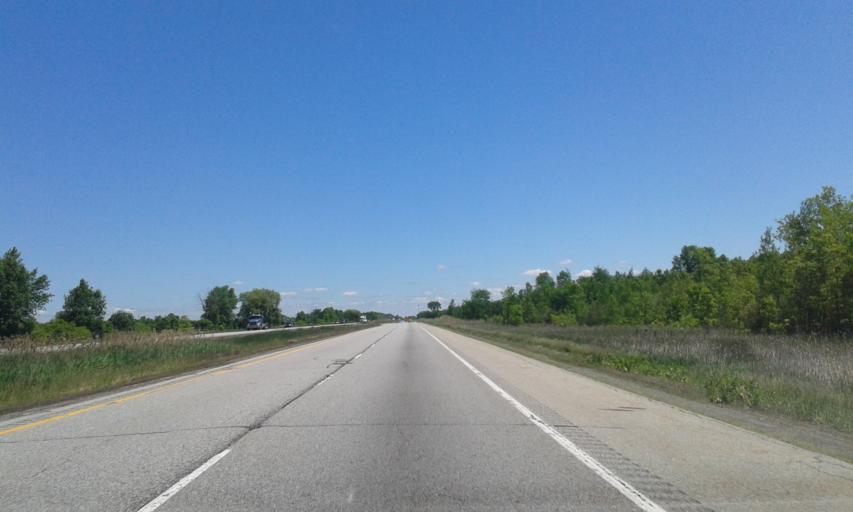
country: US
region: New York
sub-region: St. Lawrence County
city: Ogdensburg
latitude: 44.8728
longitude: -75.3002
